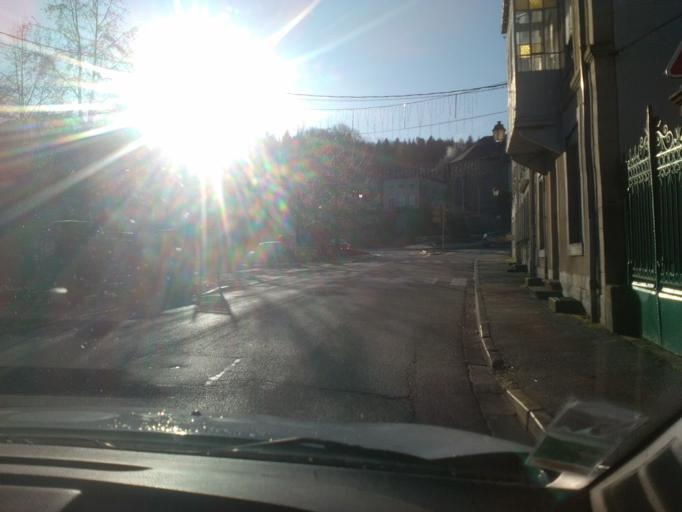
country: FR
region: Lorraine
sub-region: Departement des Vosges
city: Xertigny
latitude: 48.0456
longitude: 6.4022
